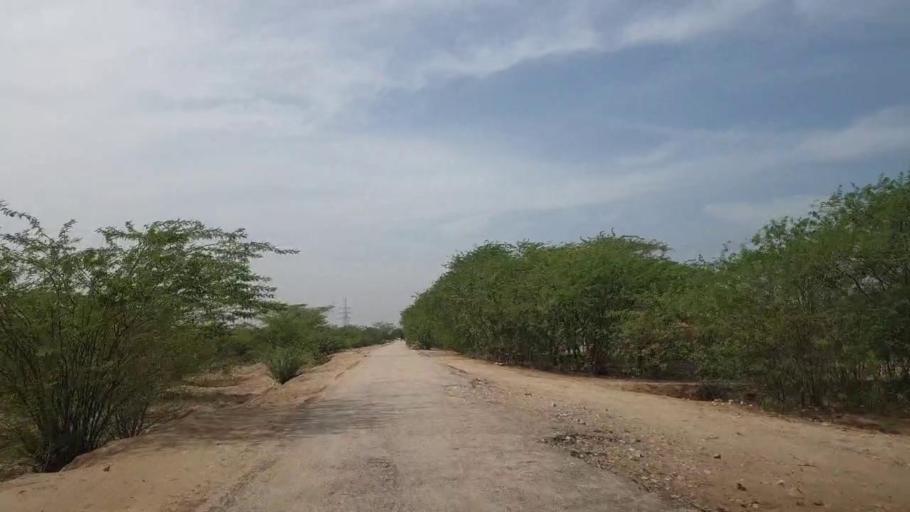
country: PK
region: Sindh
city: Kot Diji
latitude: 27.3660
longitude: 68.7642
